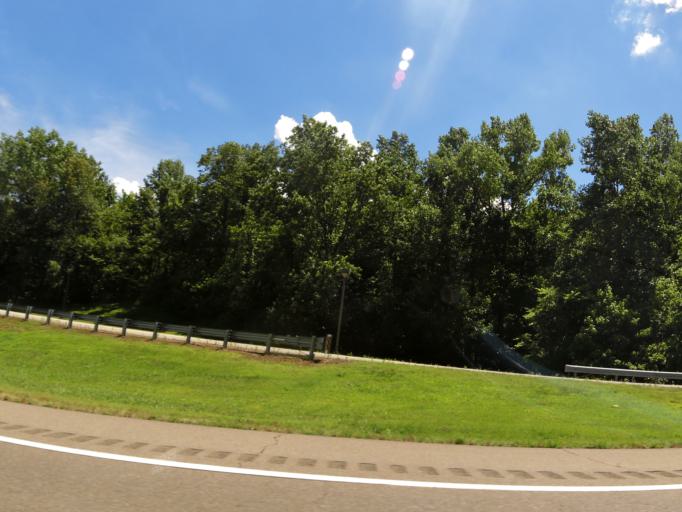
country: US
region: Tennessee
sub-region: Dyer County
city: Dyersburg
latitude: 36.0727
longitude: -89.4735
